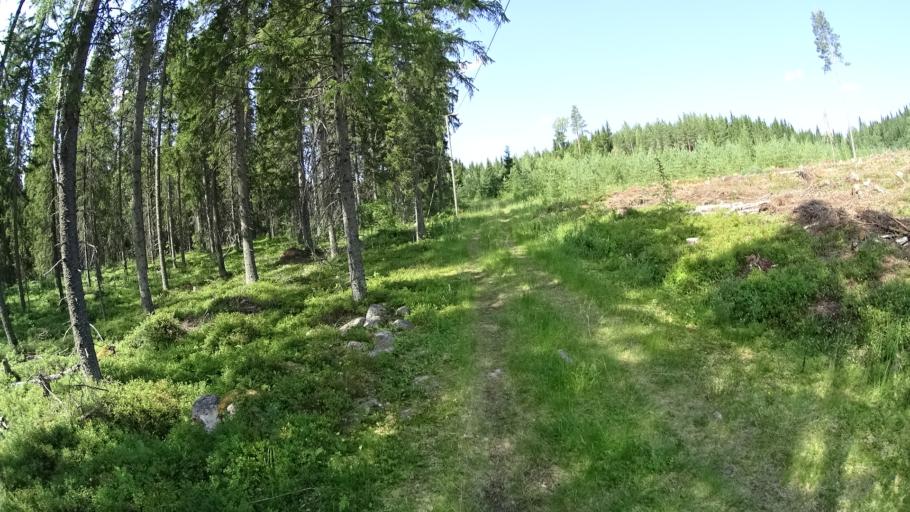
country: FI
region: North Karelia
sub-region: Pielisen Karjala
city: Lieksa
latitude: 63.1243
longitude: 29.8037
